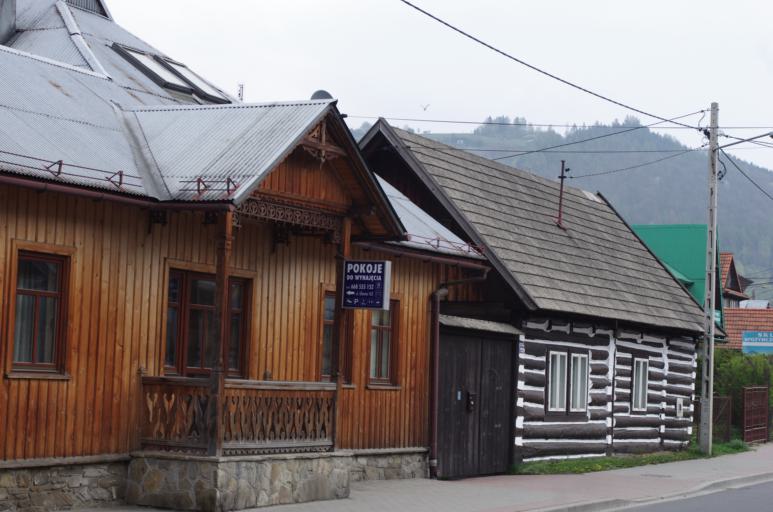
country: PL
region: Lesser Poland Voivodeship
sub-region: Powiat nowotarski
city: Szczawnica
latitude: 49.4255
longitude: 20.4620
